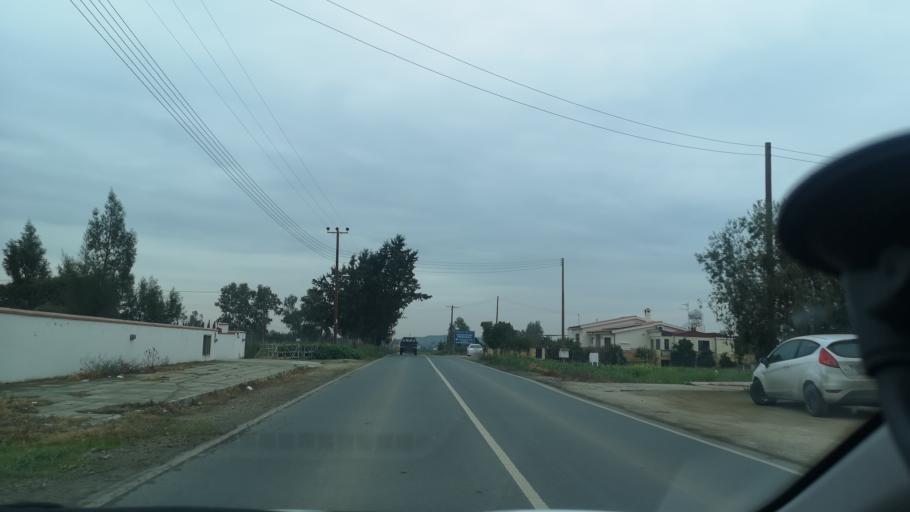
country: CY
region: Lefkosia
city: Kato Deftera
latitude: 35.0829
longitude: 33.2983
